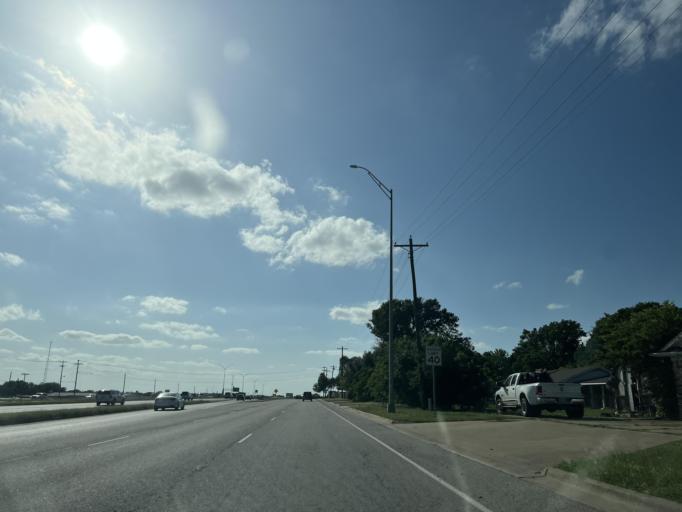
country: US
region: Texas
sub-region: Washington County
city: Brenham
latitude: 30.1456
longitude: -96.4030
